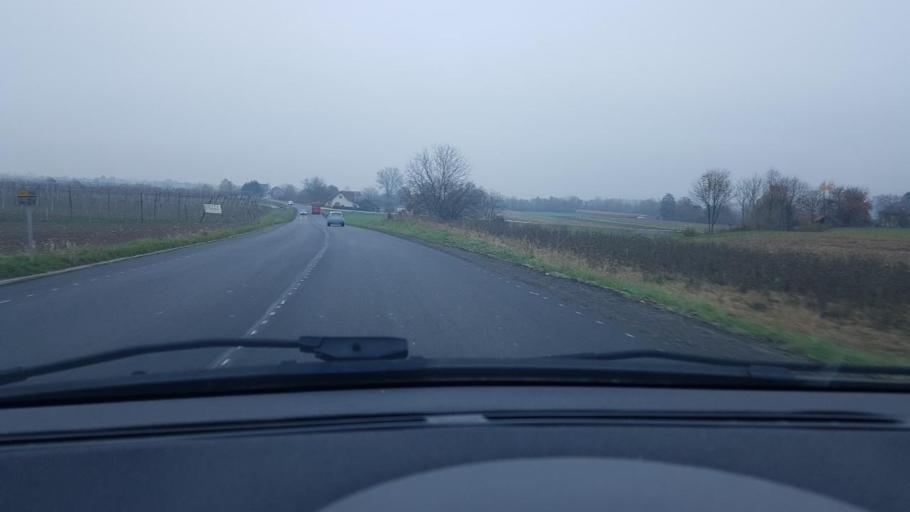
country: SI
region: Tabor
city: Tabor
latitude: 46.2464
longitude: 15.0524
